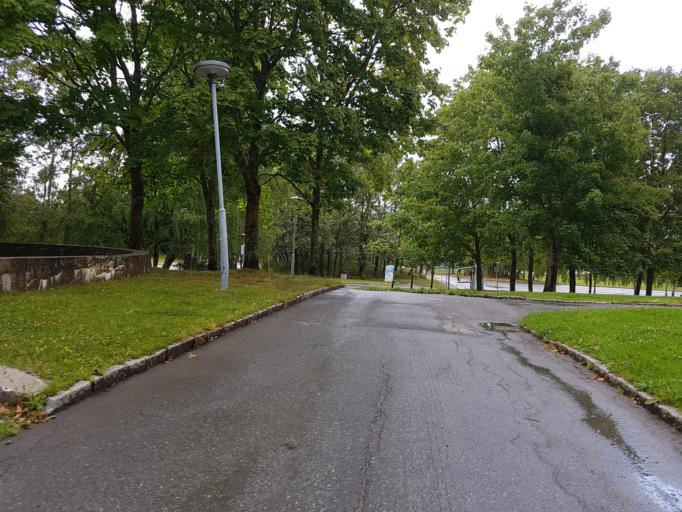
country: NO
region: Sor-Trondelag
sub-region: Trondheim
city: Trondheim
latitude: 63.4089
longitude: 10.4673
